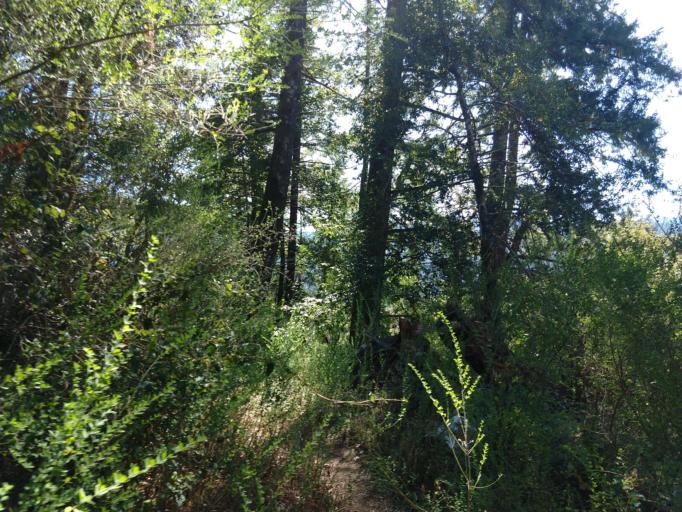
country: US
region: California
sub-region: Humboldt County
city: Rio Dell
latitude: 40.3587
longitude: -123.9977
